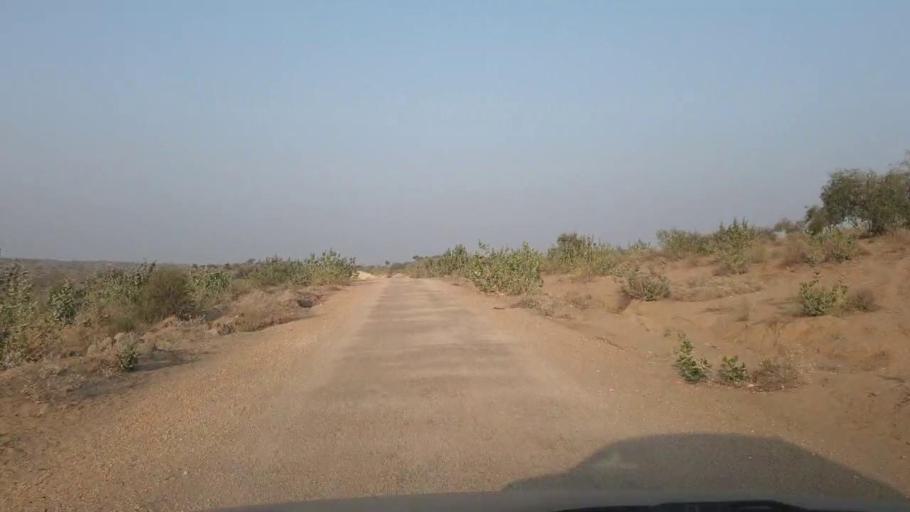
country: PK
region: Sindh
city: Umarkot
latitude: 25.2521
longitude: 69.9079
